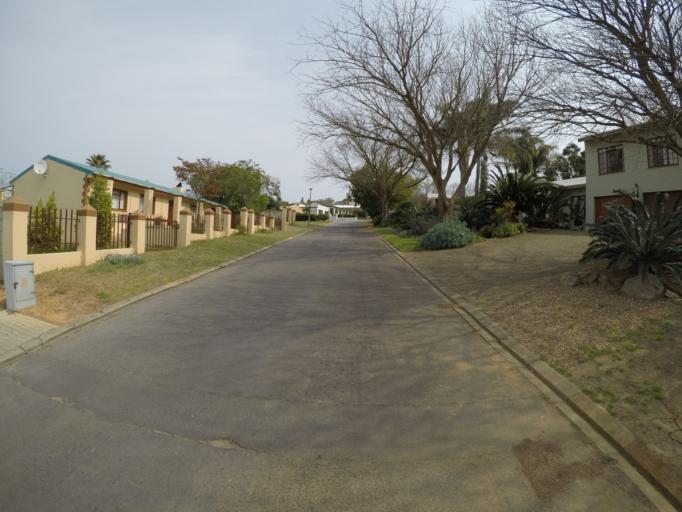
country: ZA
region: Western Cape
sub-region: West Coast District Municipality
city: Malmesbury
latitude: -33.4617
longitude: 18.7397
